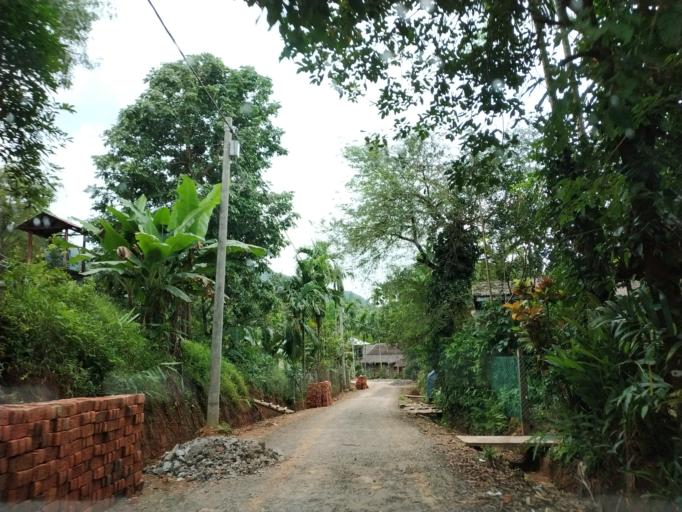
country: MM
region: Tanintharyi
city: Dawei
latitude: 13.8619
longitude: 98.2669
